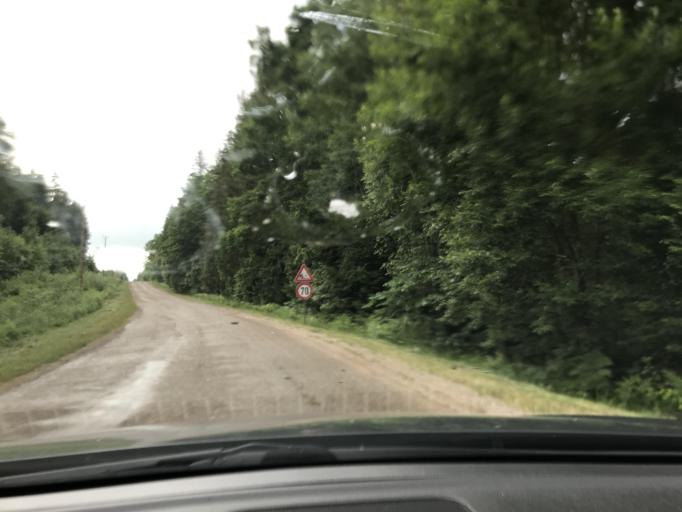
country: LV
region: Alsunga
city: Alsunga
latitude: 56.9860
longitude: 21.6305
